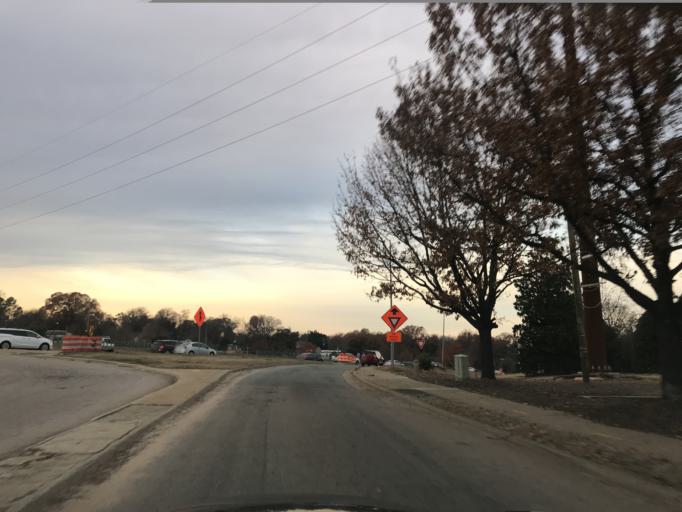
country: US
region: North Carolina
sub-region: Wake County
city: Raleigh
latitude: 35.7885
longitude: -78.6422
